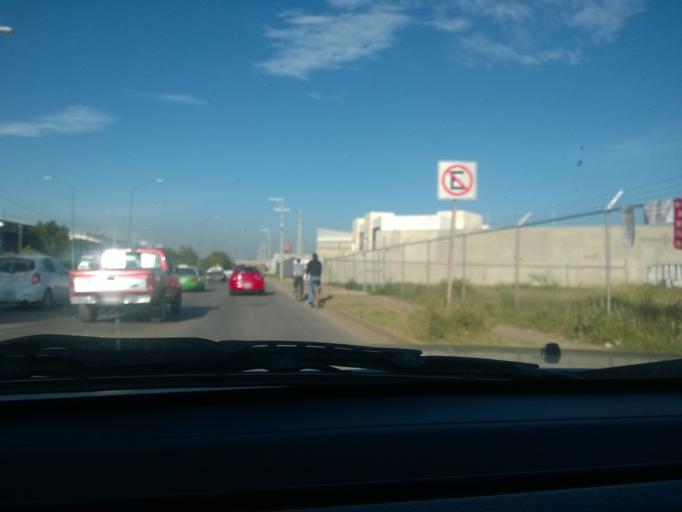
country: MX
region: Guanajuato
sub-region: Leon
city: Medina
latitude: 21.1251
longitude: -101.6234
